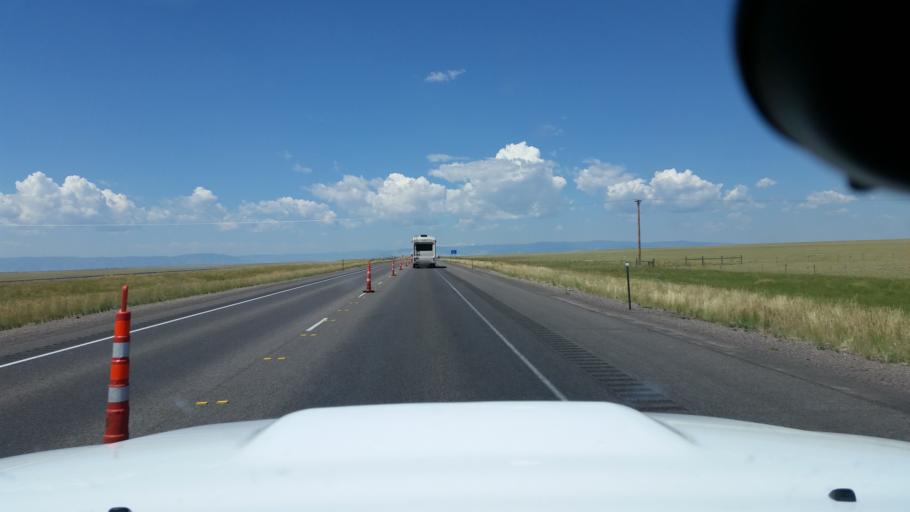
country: US
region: Wyoming
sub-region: Albany County
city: Laramie
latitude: 41.3510
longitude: -105.6516
